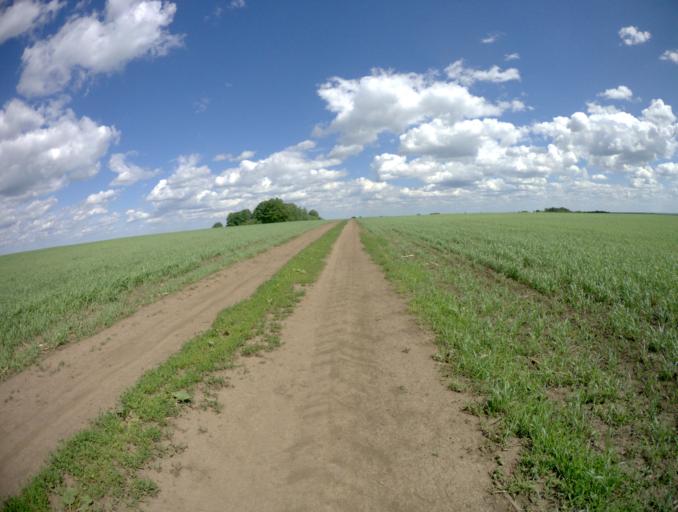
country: RU
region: Vladimir
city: Suzdal'
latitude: 56.4289
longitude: 40.2926
